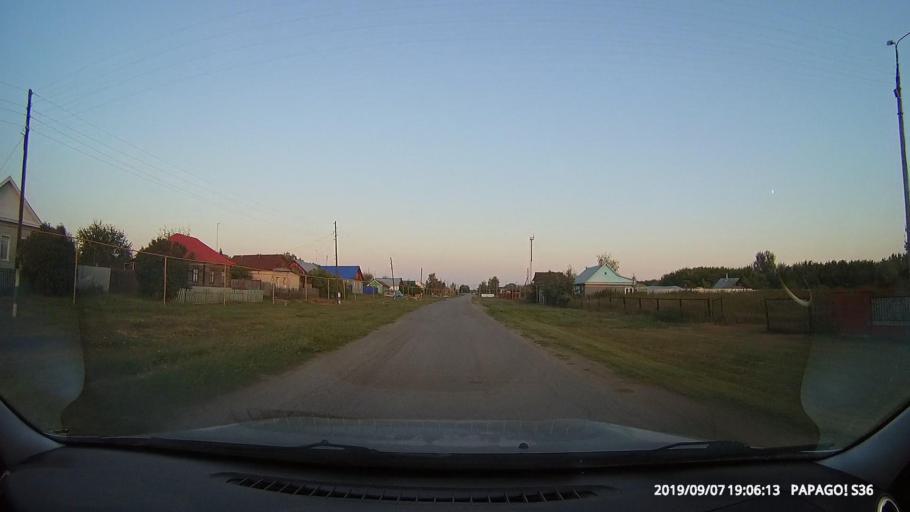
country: RU
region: Samara
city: Chapayevsk
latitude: 52.9908
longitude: 49.7769
